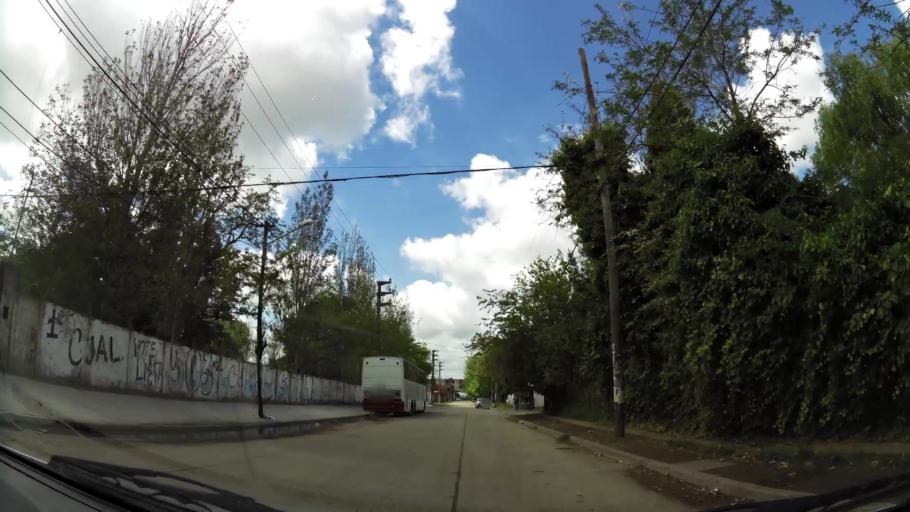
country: AR
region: Buenos Aires
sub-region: Partido de Quilmes
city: Quilmes
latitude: -34.8303
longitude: -58.2215
